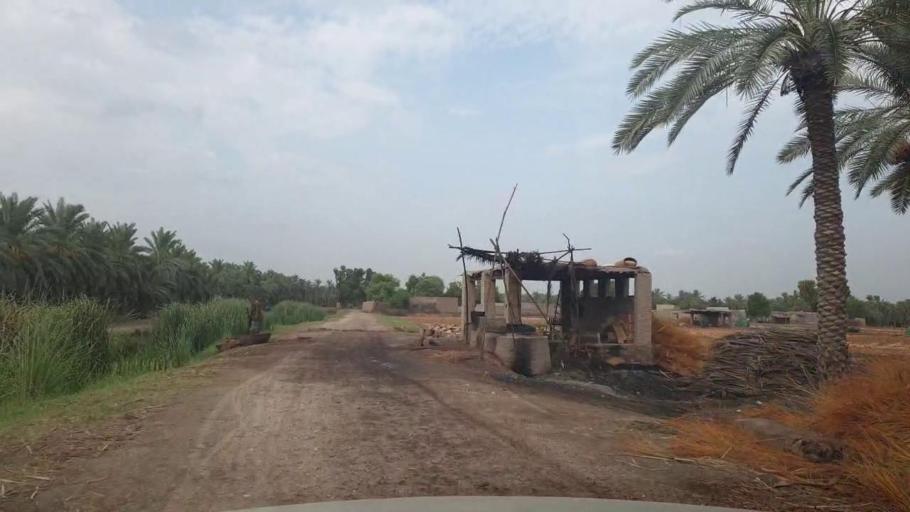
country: PK
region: Sindh
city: Khairpur
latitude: 27.6021
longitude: 68.8296
